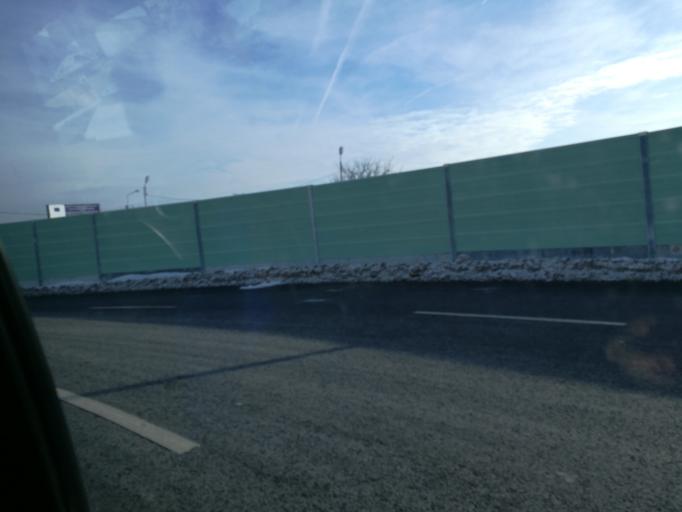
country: RO
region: Ilfov
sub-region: Comuna Fundeni-Dobroesti
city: Fundeni
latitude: 44.4784
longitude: 26.1378
